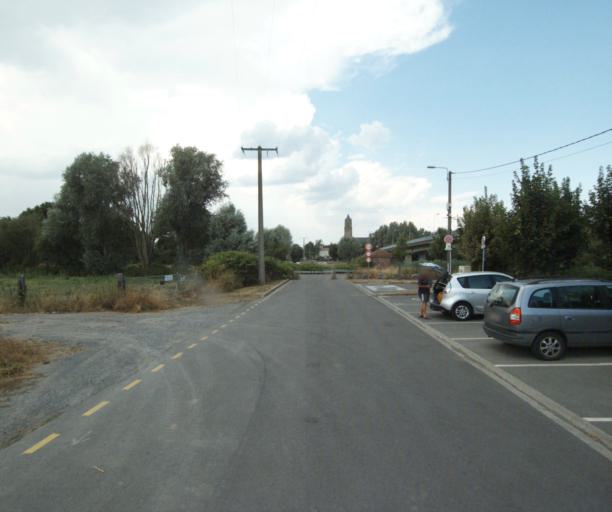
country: FR
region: Nord-Pas-de-Calais
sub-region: Departement du Nord
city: Deulemont
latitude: 50.7492
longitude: 2.9521
